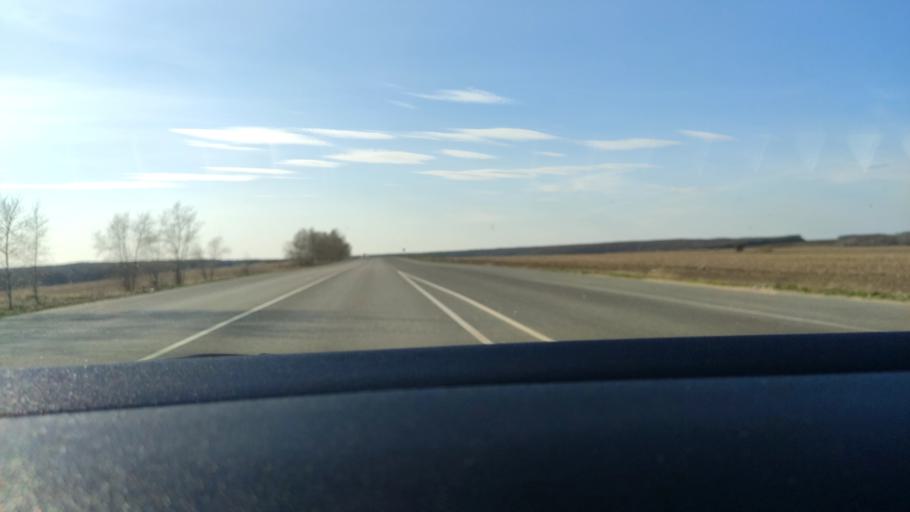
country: RU
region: Voronezj
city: Kolodeznyy
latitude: 51.3339
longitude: 39.0886
